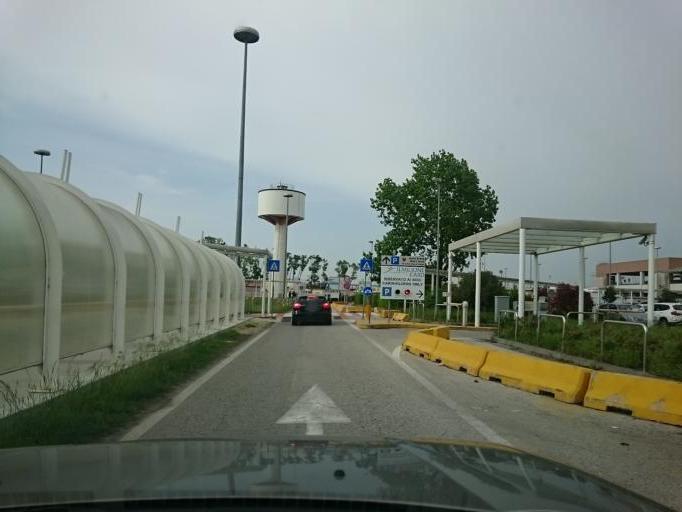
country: IT
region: Veneto
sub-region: Provincia di Venezia
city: Tessera
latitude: 45.5039
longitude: 12.3380
